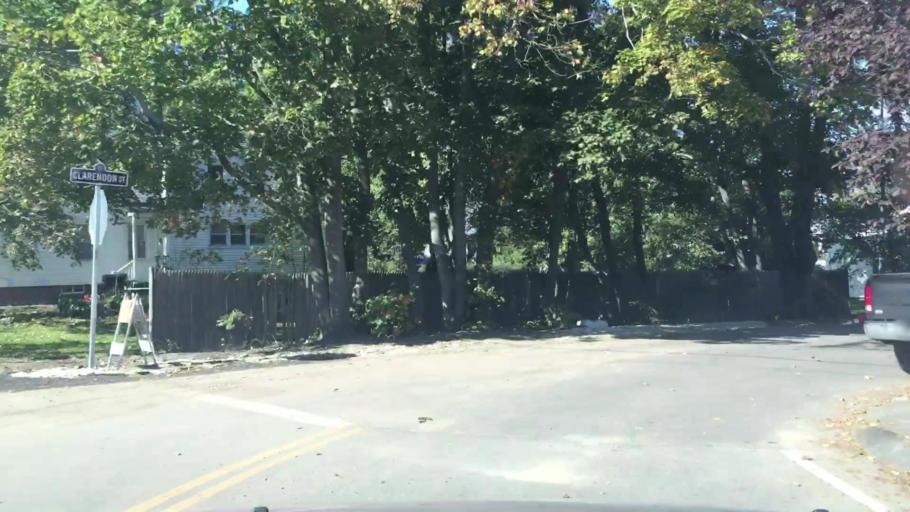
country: US
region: Massachusetts
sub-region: Essex County
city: North Andover
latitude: 42.6983
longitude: -71.1226
